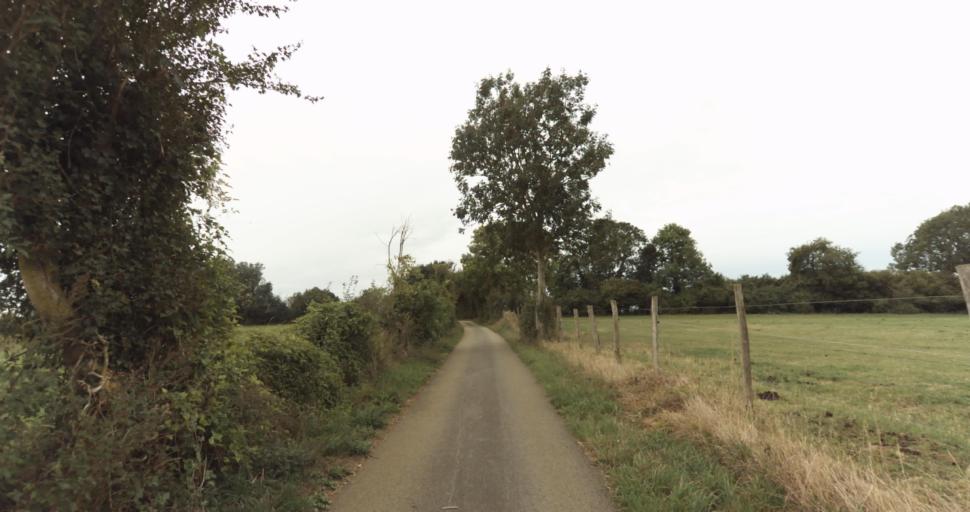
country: FR
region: Lower Normandy
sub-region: Departement de l'Orne
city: Gace
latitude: 48.7617
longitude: 0.3229
